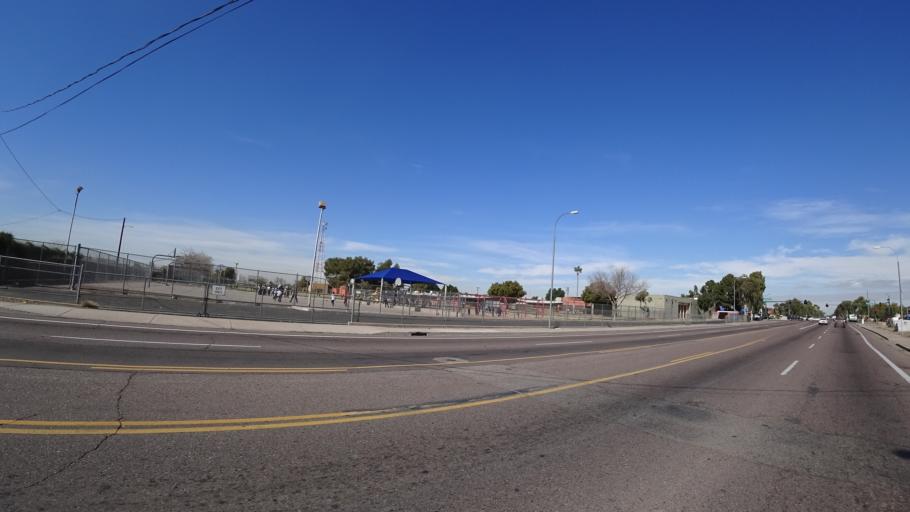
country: US
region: Arizona
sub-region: Maricopa County
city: Tolleson
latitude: 33.4500
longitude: -112.2034
